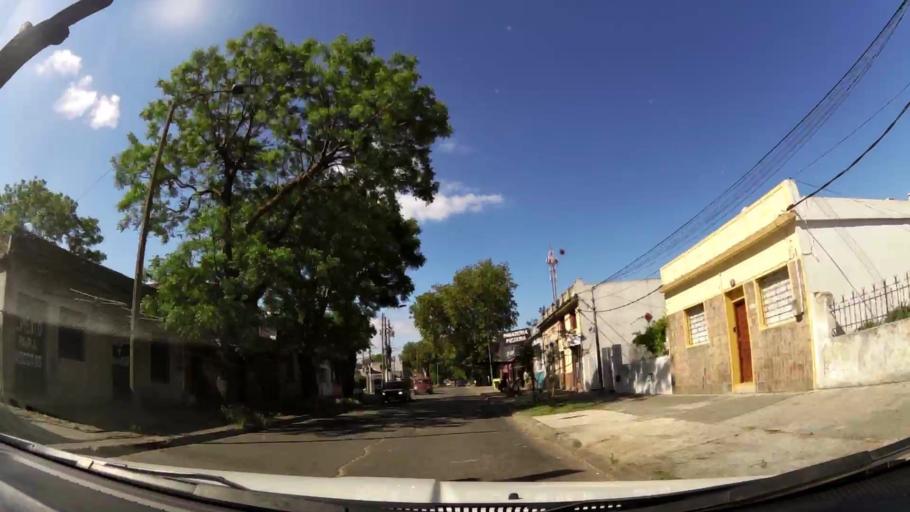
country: UY
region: Montevideo
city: Montevideo
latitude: -34.8472
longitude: -56.2130
